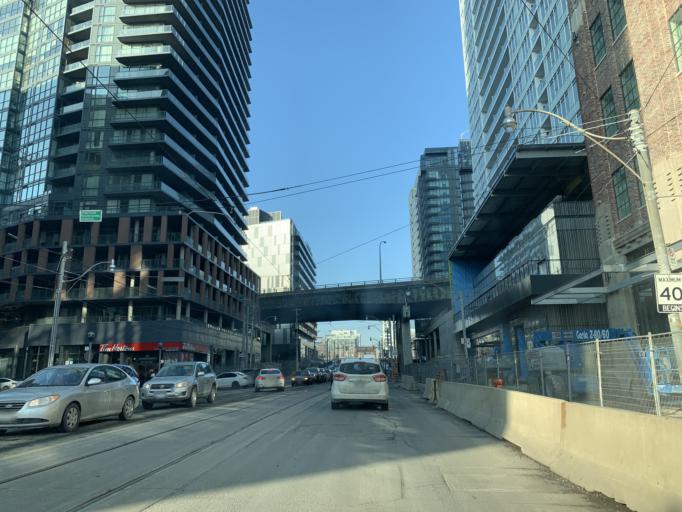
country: CA
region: Ontario
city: Toronto
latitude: 43.6370
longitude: -79.3999
